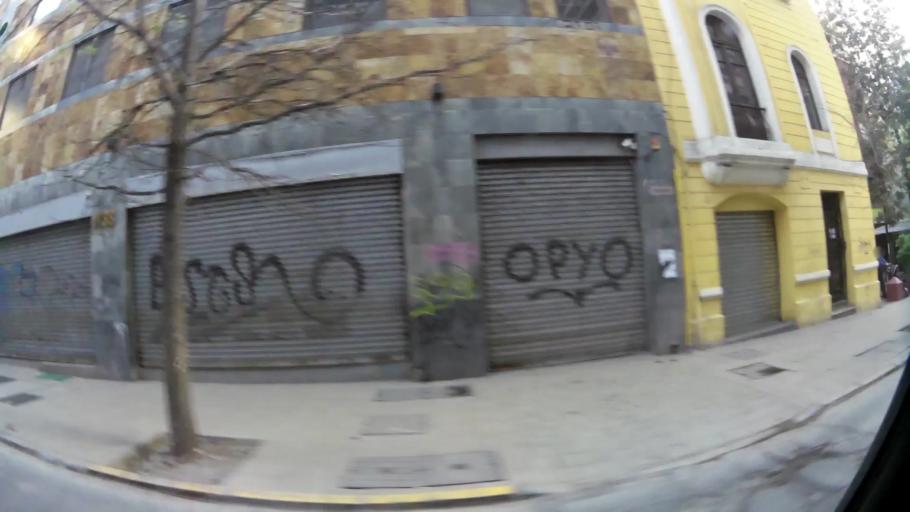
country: CL
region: Santiago Metropolitan
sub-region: Provincia de Santiago
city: Santiago
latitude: -33.4365
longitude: -70.6533
